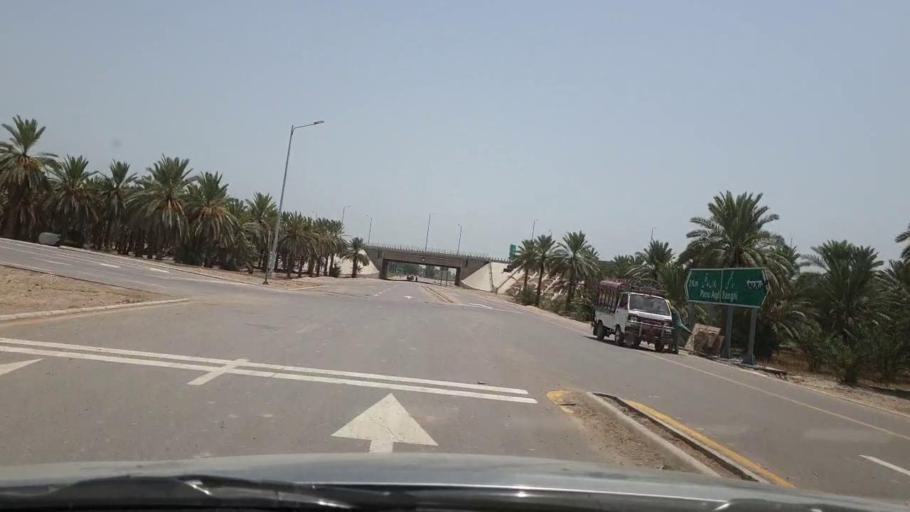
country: PK
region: Sindh
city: Pano Aqil
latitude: 27.8604
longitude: 69.0810
